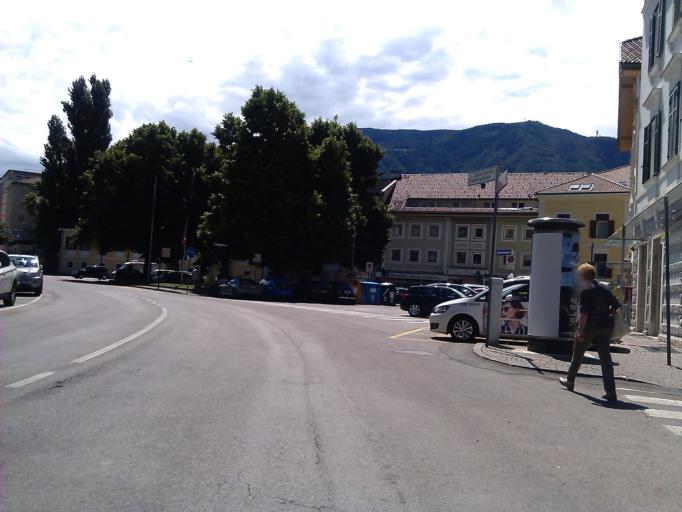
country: IT
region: Trentino-Alto Adige
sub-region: Bolzano
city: Bolzano
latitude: 46.5026
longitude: 11.3347
